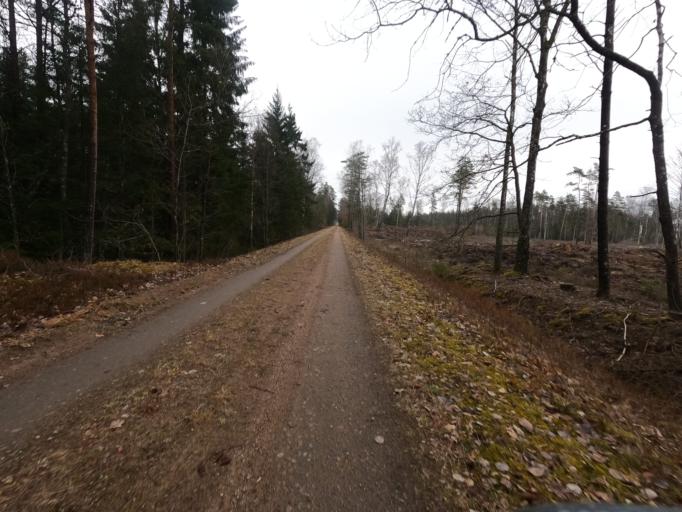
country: SE
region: Kronoberg
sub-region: Markaryds Kommun
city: Stromsnasbruk
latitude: 56.7918
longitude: 13.6651
